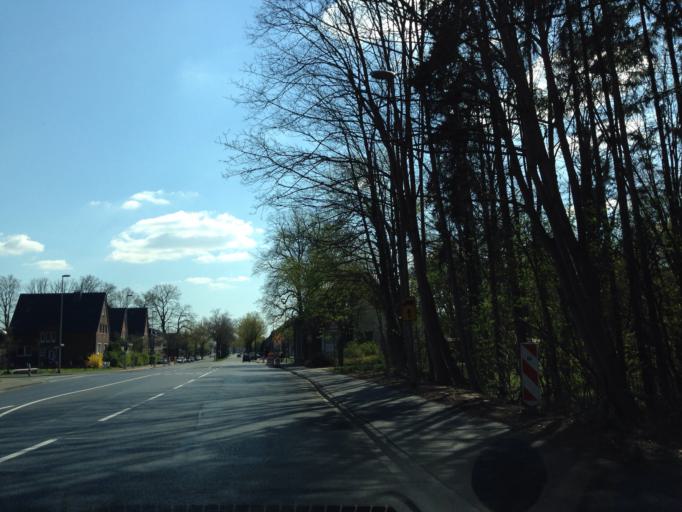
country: DE
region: North Rhine-Westphalia
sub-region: Regierungsbezirk Munster
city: Muenster
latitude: 52.0024
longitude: 7.6145
